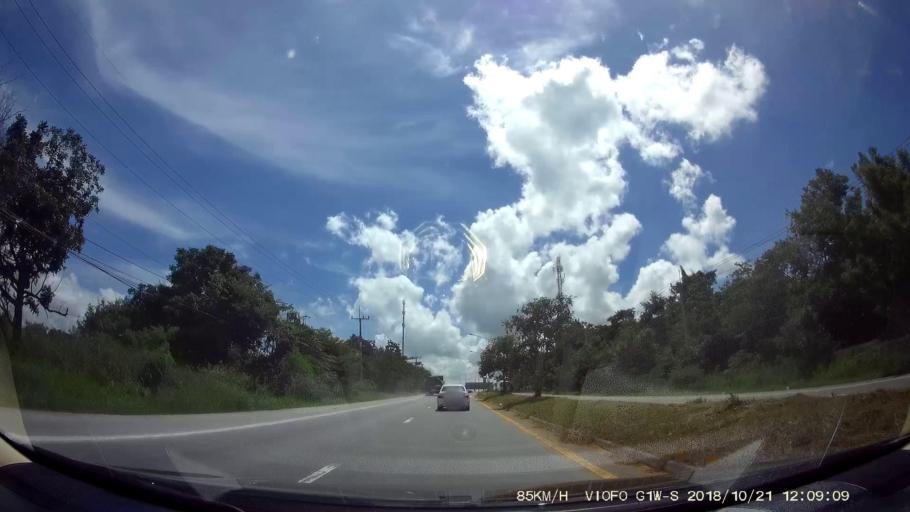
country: TH
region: Chaiyaphum
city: Chatturat
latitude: 15.4242
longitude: 101.8320
